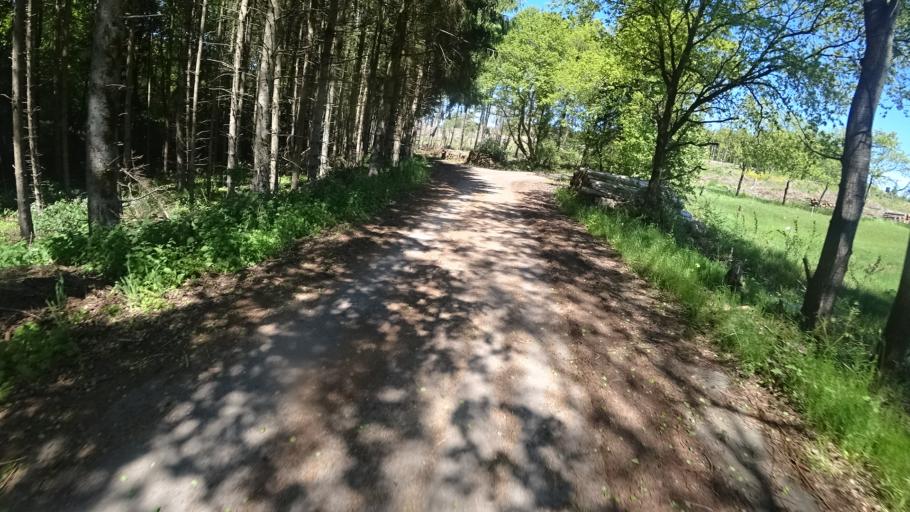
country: DE
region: Rheinland-Pfalz
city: Kausen
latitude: 50.7493
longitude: 7.8711
